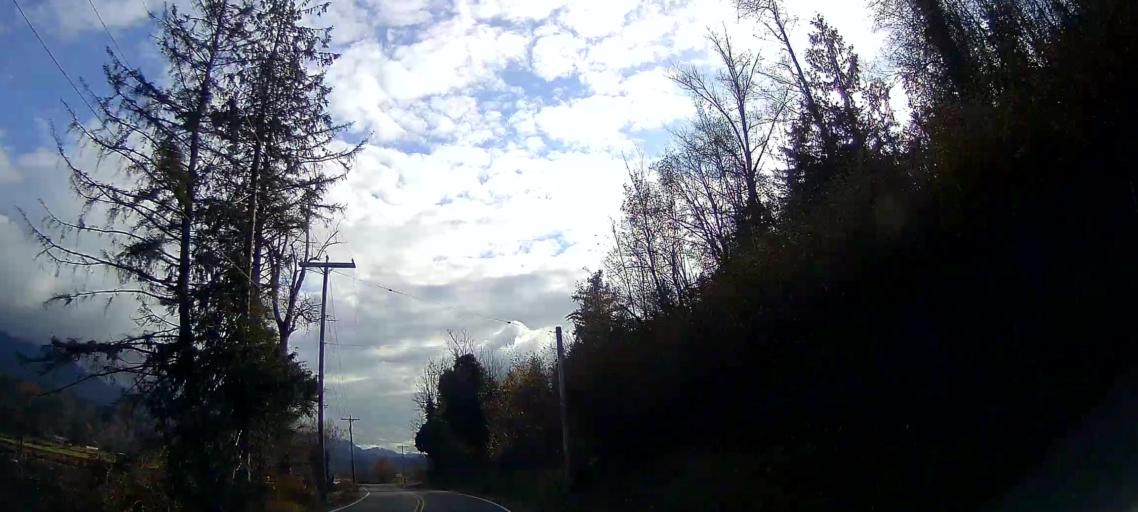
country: US
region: Washington
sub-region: Skagit County
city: Clear Lake
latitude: 48.4467
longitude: -122.2220
